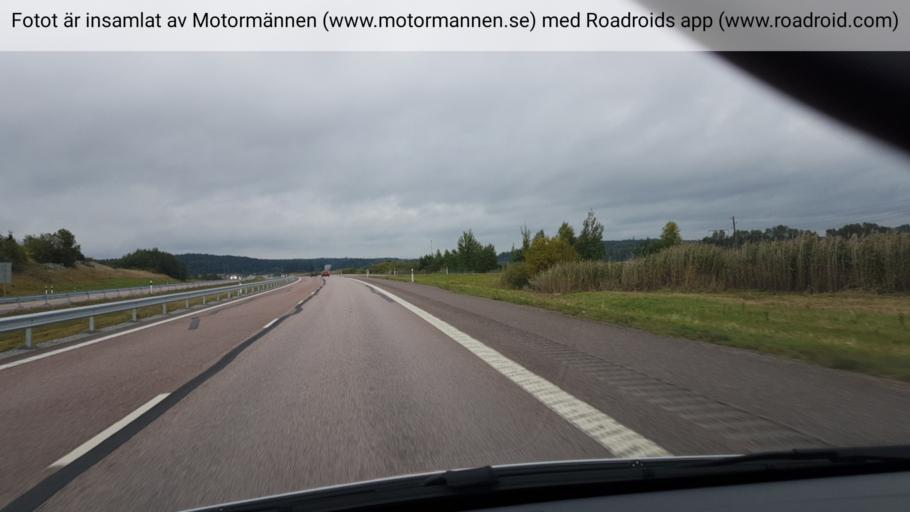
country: SE
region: Soedermanland
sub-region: Strangnas Kommun
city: Akers Styckebruk
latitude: 59.2785
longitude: 17.1131
